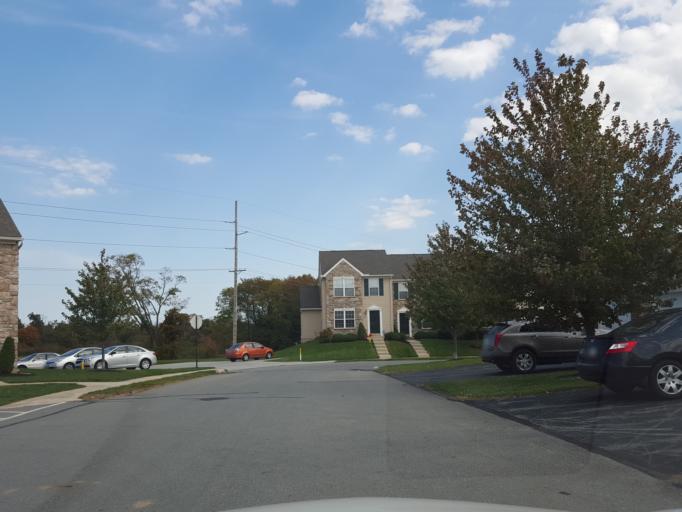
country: US
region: Pennsylvania
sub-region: York County
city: Yoe
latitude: 39.9214
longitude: -76.6248
